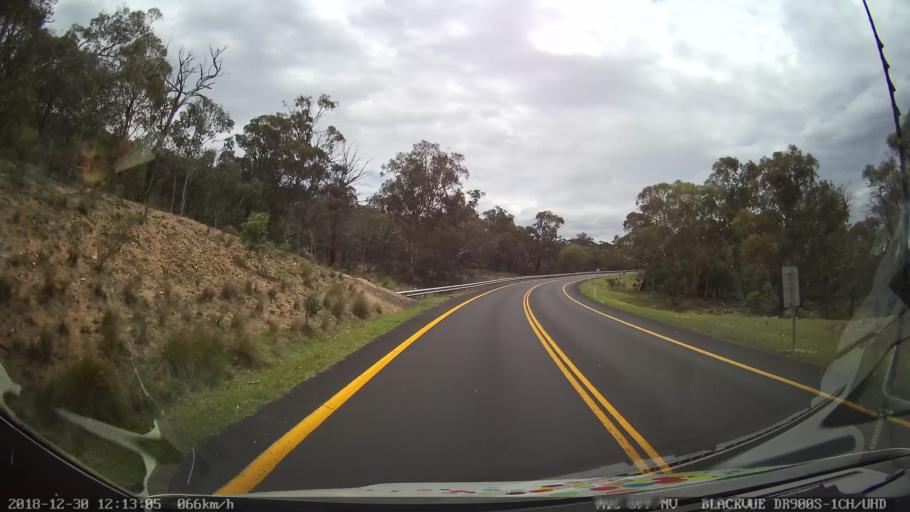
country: AU
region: New South Wales
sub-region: Snowy River
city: Jindabyne
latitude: -36.3517
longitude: 148.5856
